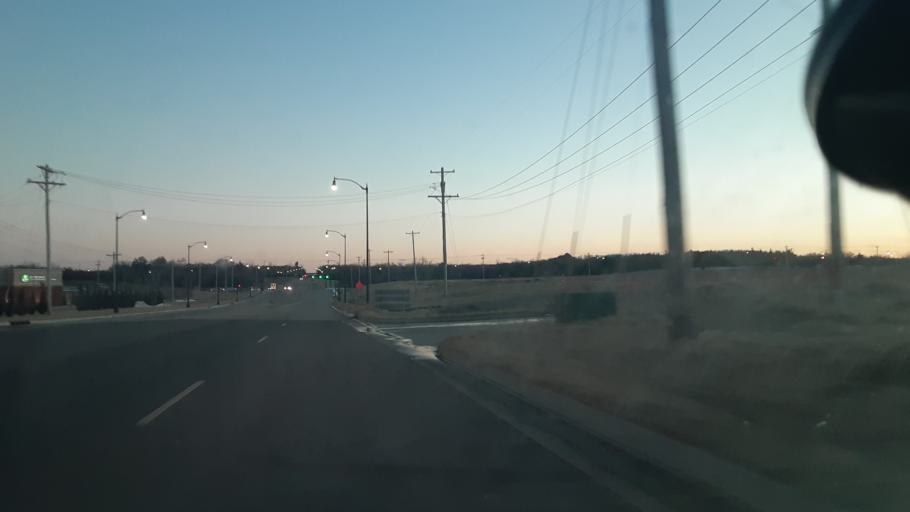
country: US
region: Oklahoma
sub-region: Oklahoma County
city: Edmond
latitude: 35.6849
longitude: -97.4252
